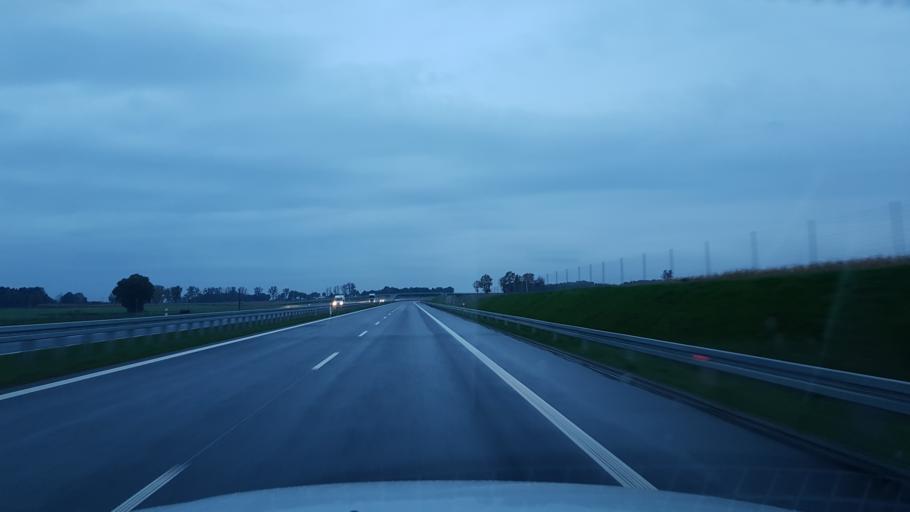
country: PL
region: West Pomeranian Voivodeship
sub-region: Powiat gryficki
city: Brojce
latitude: 53.9015
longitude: 15.3823
